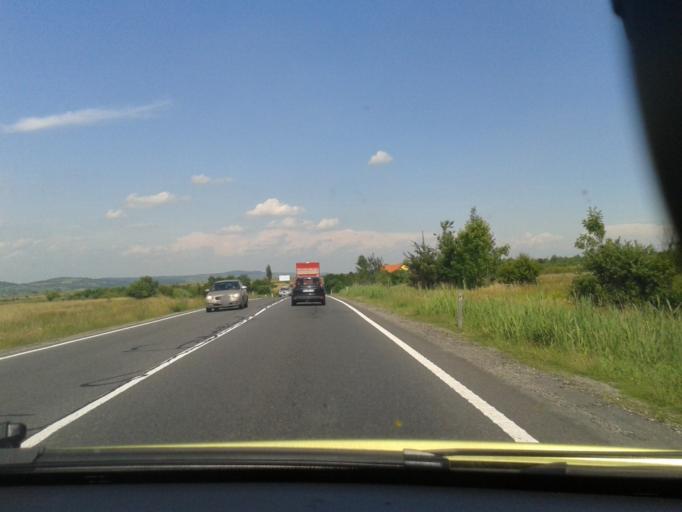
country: RO
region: Sibiu
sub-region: Comuna Carta
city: Carta
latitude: 45.7587
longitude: 24.5505
